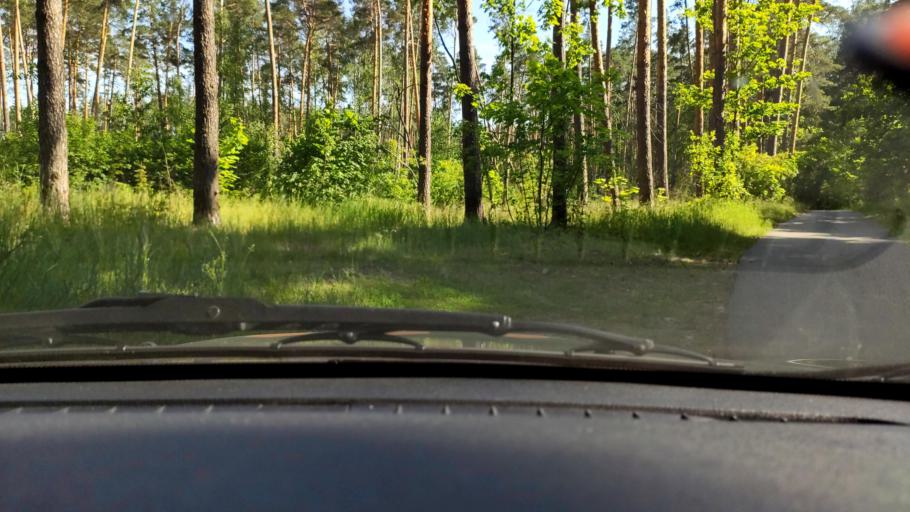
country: RU
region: Voronezj
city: Somovo
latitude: 51.8075
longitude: 39.3830
